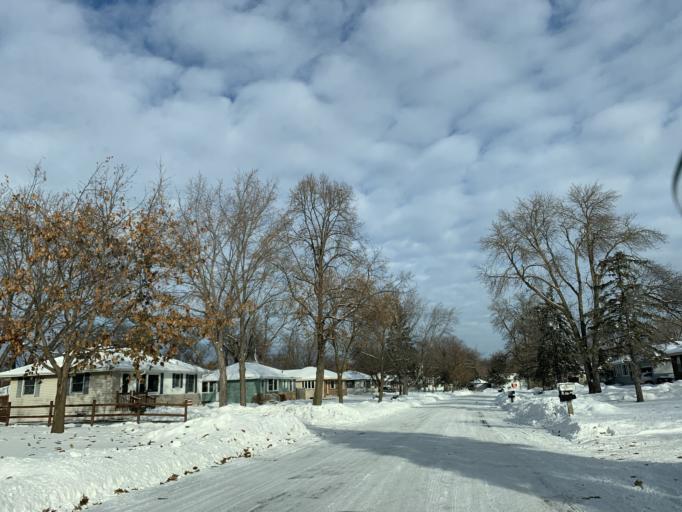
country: US
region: Minnesota
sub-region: Anoka County
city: Coon Rapids
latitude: 45.1692
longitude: -93.2873
